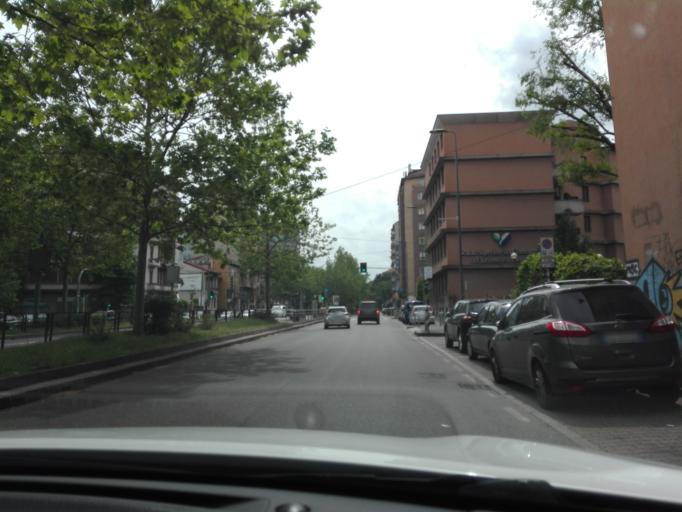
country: IT
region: Lombardy
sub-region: Citta metropolitana di Milano
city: Romano Banco
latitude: 45.4739
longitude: 9.1437
